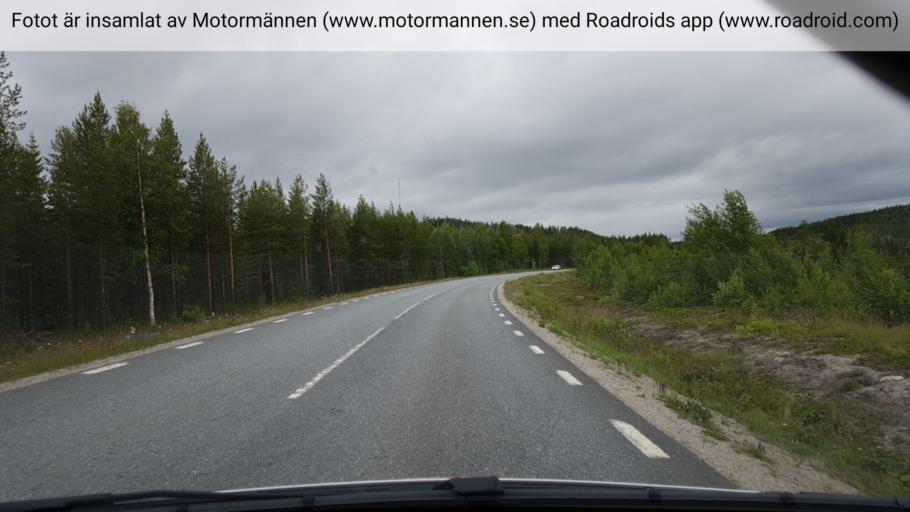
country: SE
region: Vaesterbotten
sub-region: Lycksele Kommun
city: Lycksele
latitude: 64.4791
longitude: 18.9022
